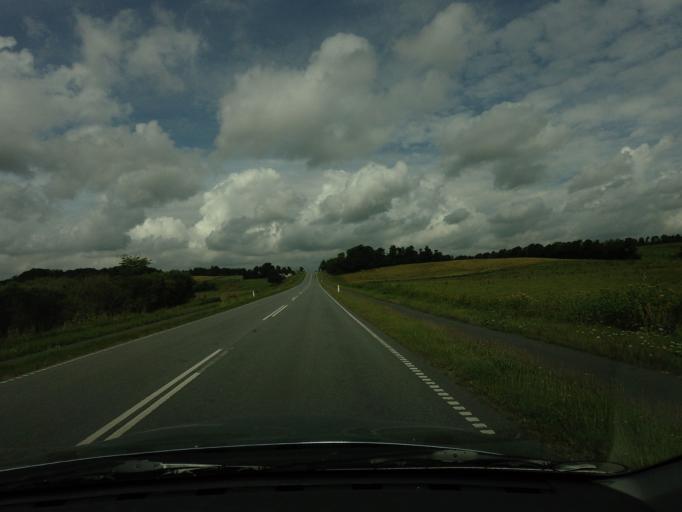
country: DK
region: North Denmark
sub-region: Hjorring Kommune
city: Tars
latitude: 57.3750
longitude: 10.1614
